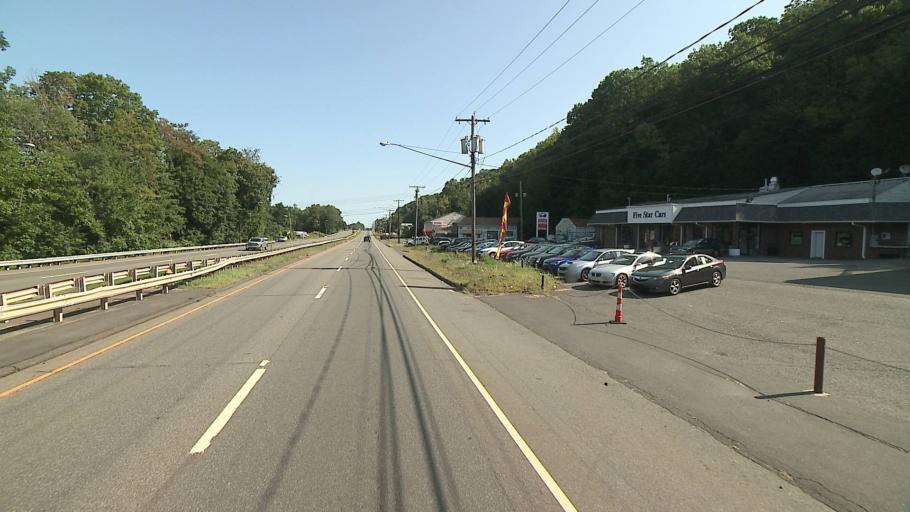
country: US
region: Connecticut
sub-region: New Haven County
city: Meriden
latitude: 41.5662
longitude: -72.7737
